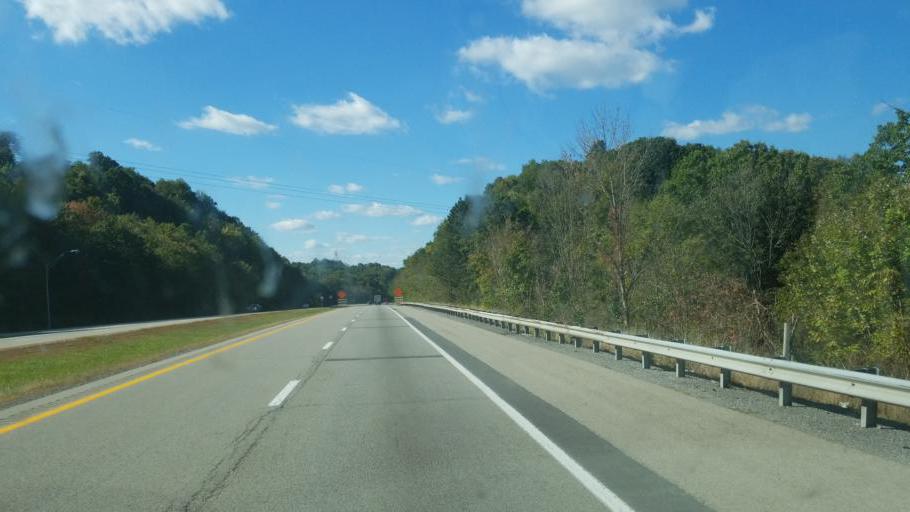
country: US
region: West Virginia
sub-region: Monongalia County
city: Star City
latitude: 39.7001
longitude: -80.0479
